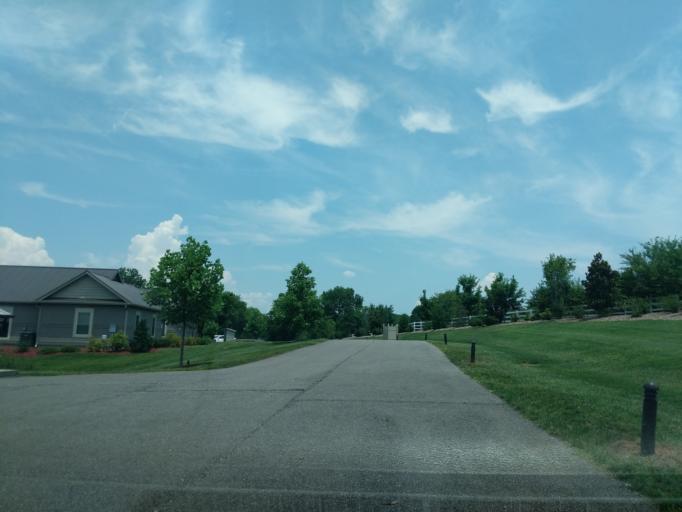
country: US
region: Tennessee
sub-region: Davidson County
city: Lakewood
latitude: 36.2325
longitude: -86.6352
